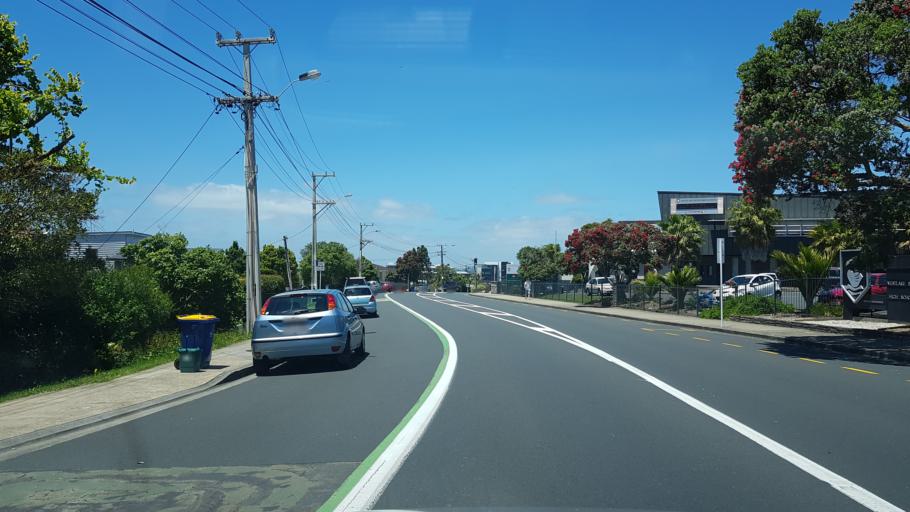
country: NZ
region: Auckland
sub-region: Auckland
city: North Shore
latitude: -36.7763
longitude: 174.7494
